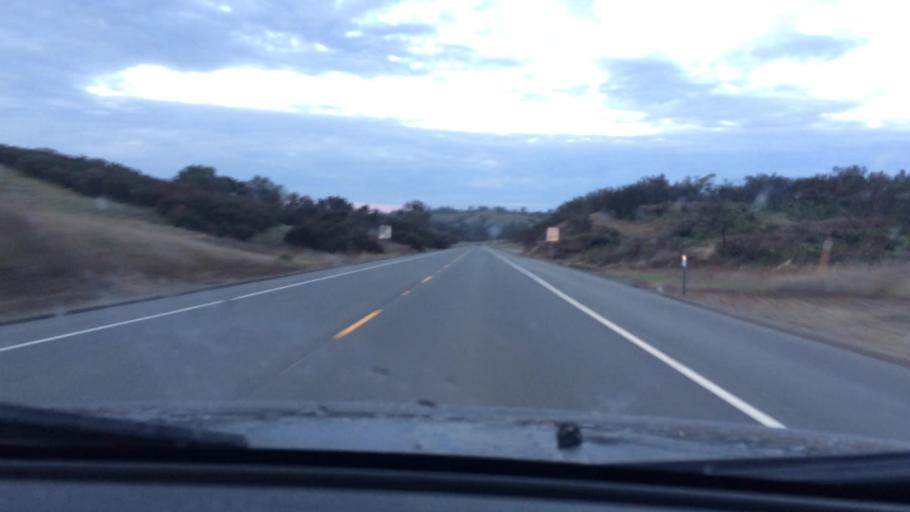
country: US
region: California
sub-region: Amador County
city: Ione
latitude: 38.3955
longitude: -120.8985
